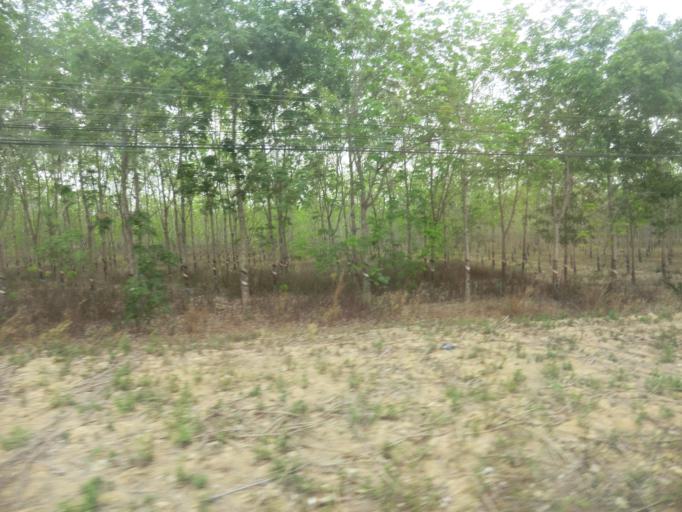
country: VN
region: Binh Thuan
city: Tanh Linh
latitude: 10.9483
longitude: 107.6524
